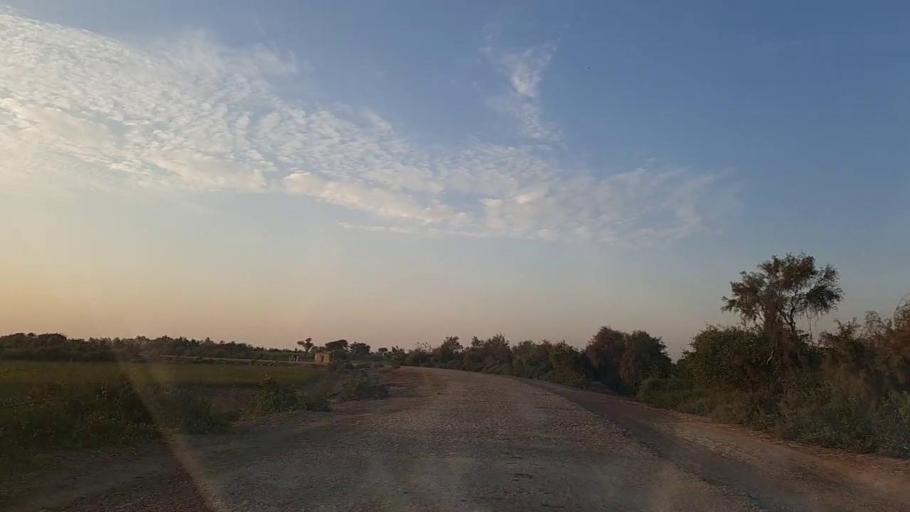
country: PK
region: Sindh
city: Chuhar Jamali
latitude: 24.4602
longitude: 68.1140
